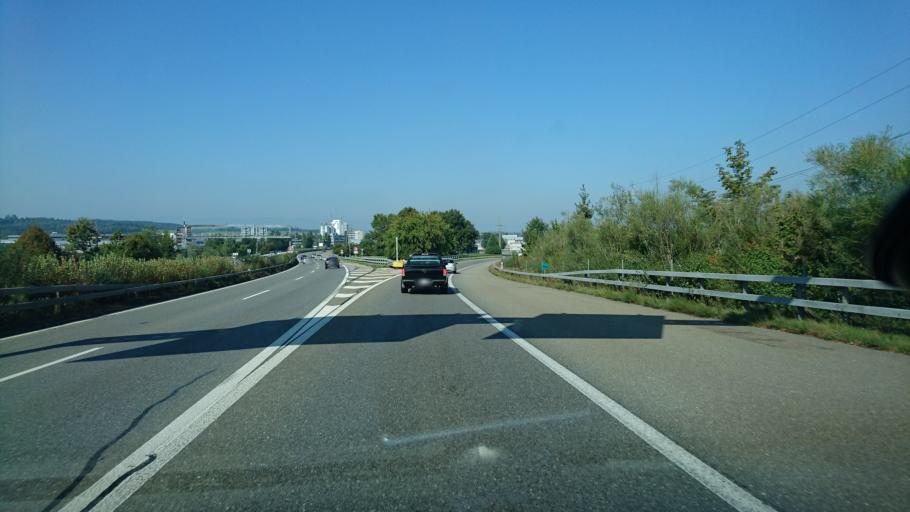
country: CH
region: Bern
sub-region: Bern-Mittelland District
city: Urtenen
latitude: 47.0105
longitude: 7.4970
